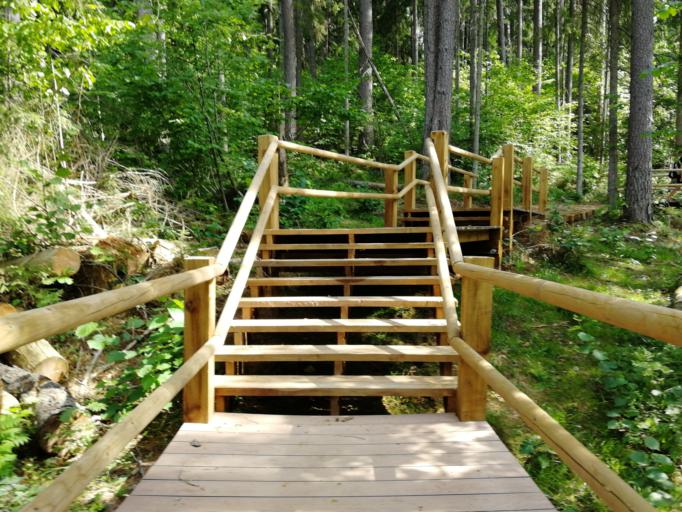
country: LV
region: Cesu Rajons
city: Cesis
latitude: 57.3021
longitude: 25.2216
